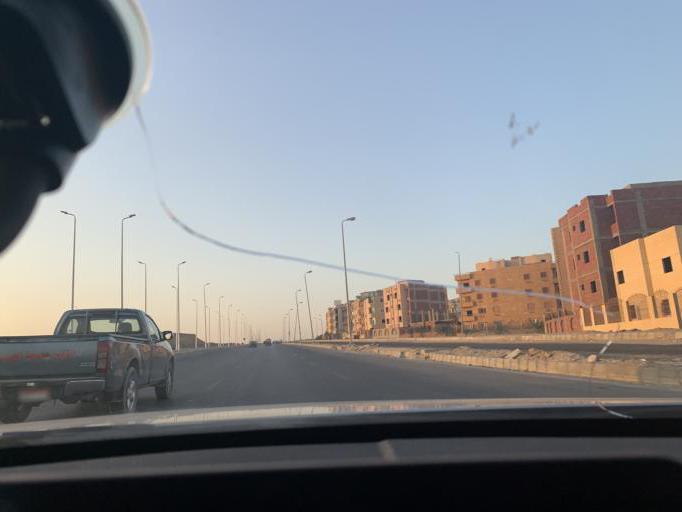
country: EG
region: Muhafazat al Qahirah
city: Halwan
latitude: 29.9806
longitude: 31.4687
